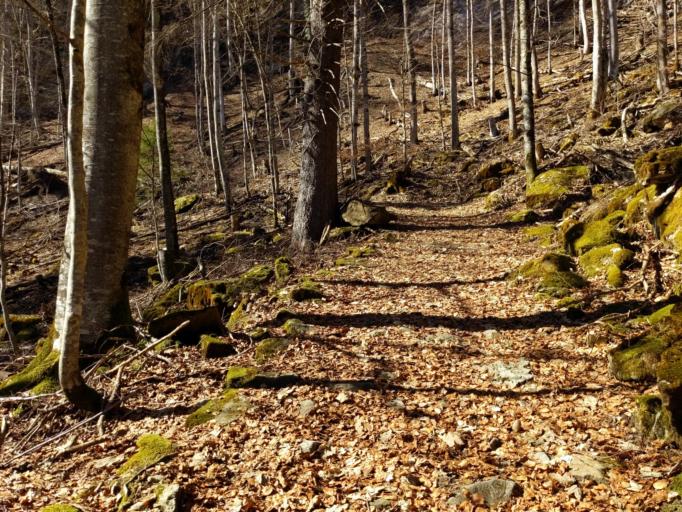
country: CH
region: Glarus
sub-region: Glarus
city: Luchsingen
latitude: 46.9482
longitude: 9.0175
